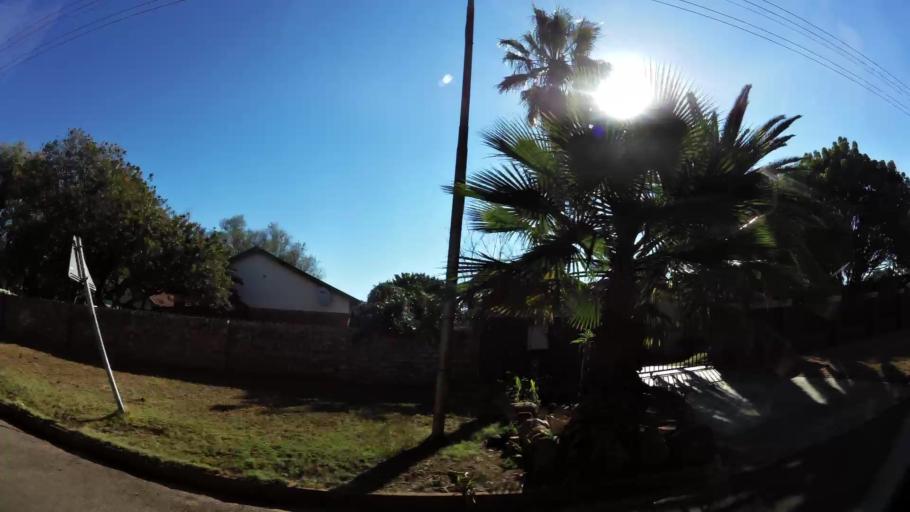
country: ZA
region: Limpopo
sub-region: Waterberg District Municipality
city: Mokopane
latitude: -24.1859
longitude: 28.9964
